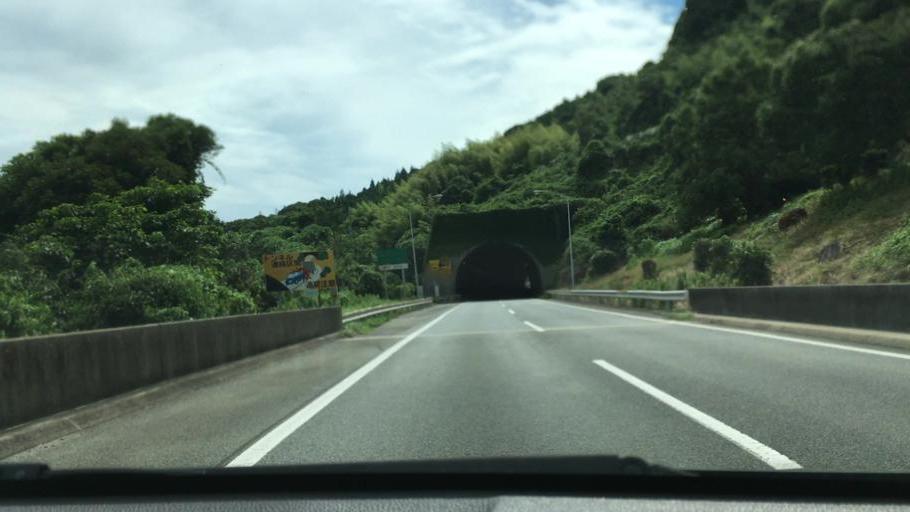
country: JP
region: Yamaguchi
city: Hofu
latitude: 34.0568
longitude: 131.6457
